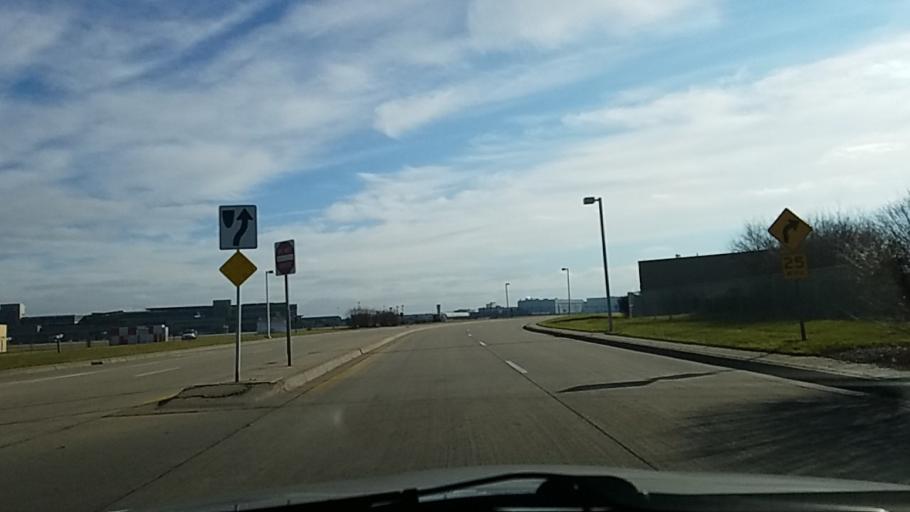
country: US
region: Minnesota
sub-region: Hennepin County
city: Richfield
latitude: 44.8789
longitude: -93.2360
